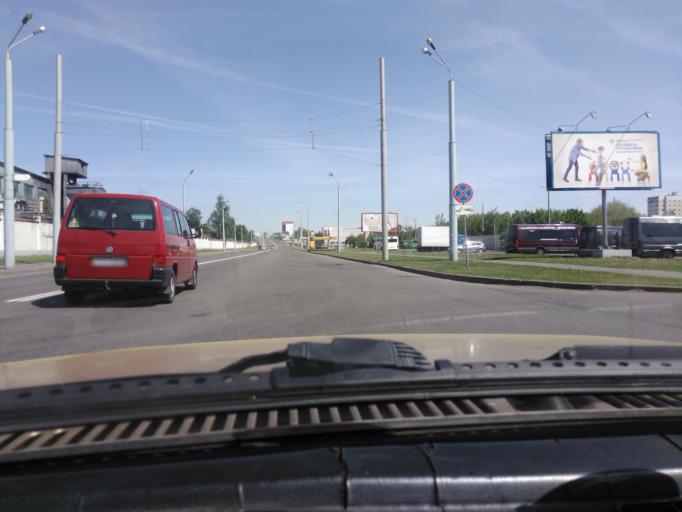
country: BY
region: Mogilev
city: Mahilyow
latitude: 53.9139
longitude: 30.3472
